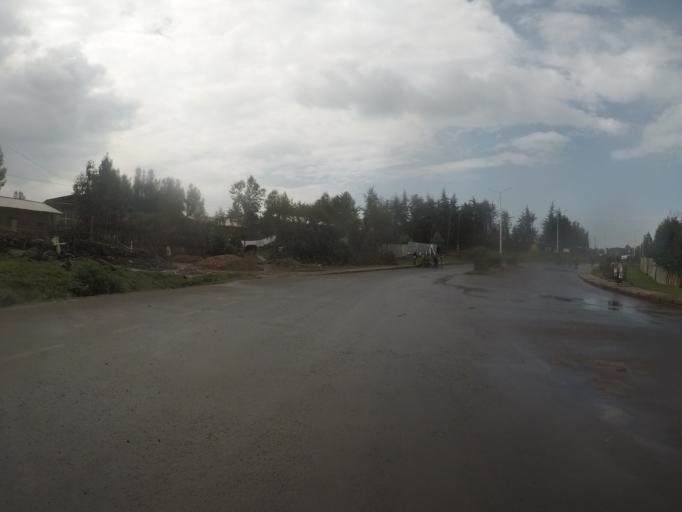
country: ET
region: Amhara
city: Debark'
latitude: 13.1406
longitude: 37.8935
